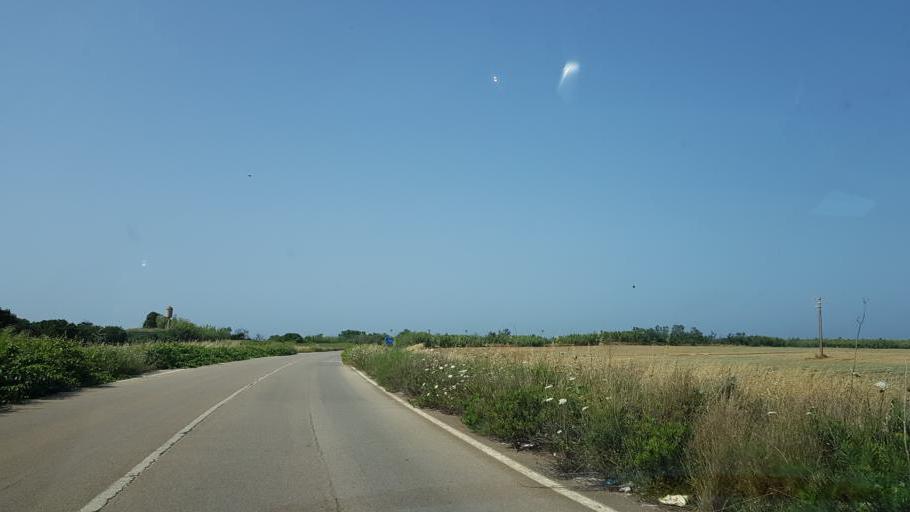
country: IT
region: Apulia
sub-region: Provincia di Brindisi
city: Materdomini
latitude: 40.6773
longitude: 17.9142
